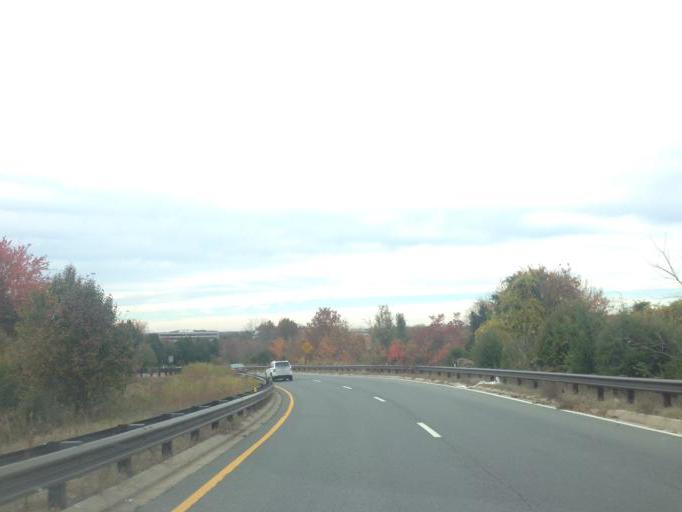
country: US
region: Maryland
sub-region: Montgomery County
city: Germantown
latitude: 39.1867
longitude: -77.2537
